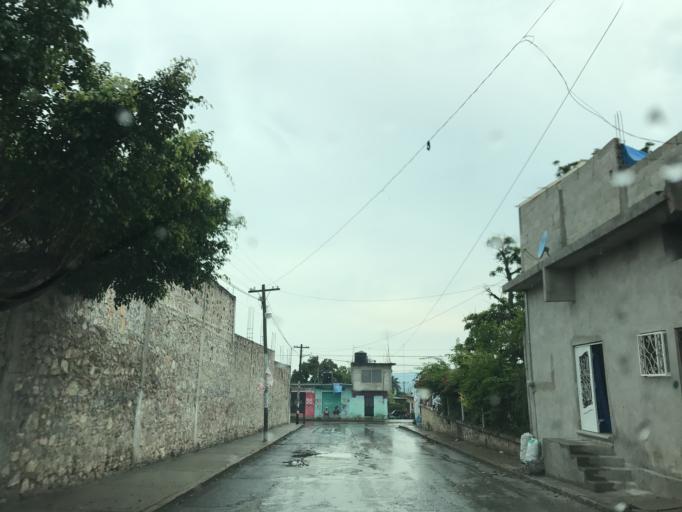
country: MX
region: Morelos
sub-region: Ayala
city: Ciudad Ayala
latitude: 18.7634
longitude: -98.9848
